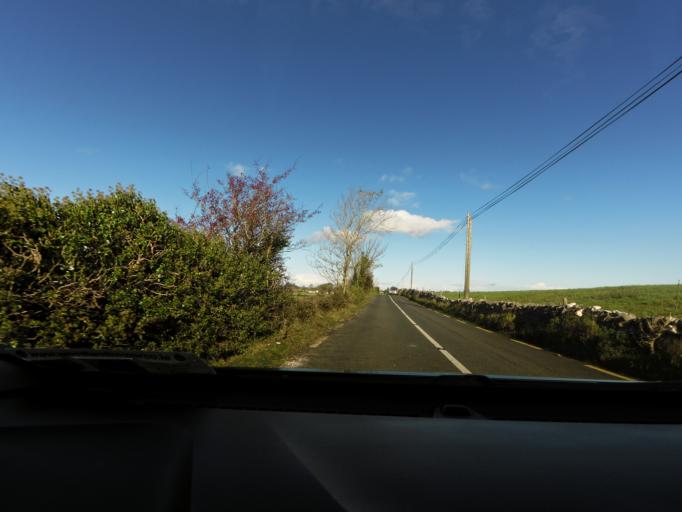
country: IE
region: Connaught
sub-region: Maigh Eo
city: Ballinrobe
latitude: 53.5519
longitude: -9.1060
